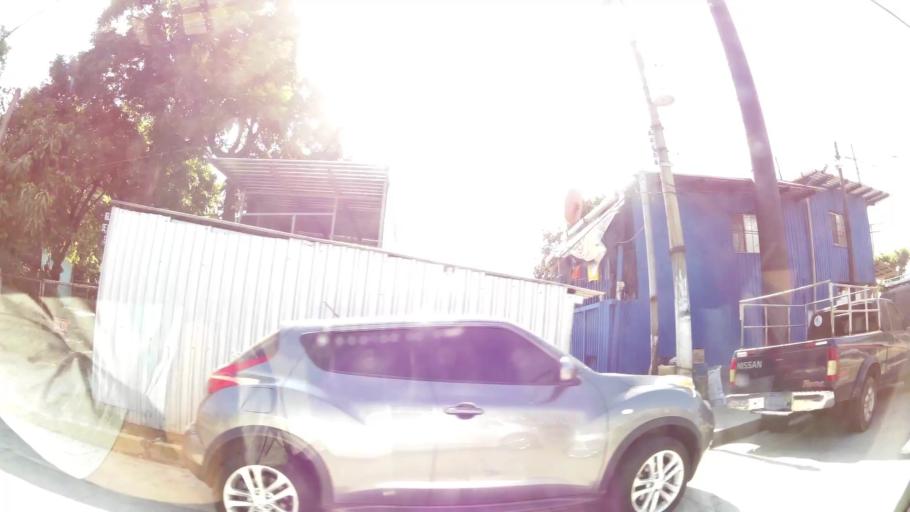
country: SV
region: La Libertad
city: Antiguo Cuscatlan
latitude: 13.6763
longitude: -89.2522
